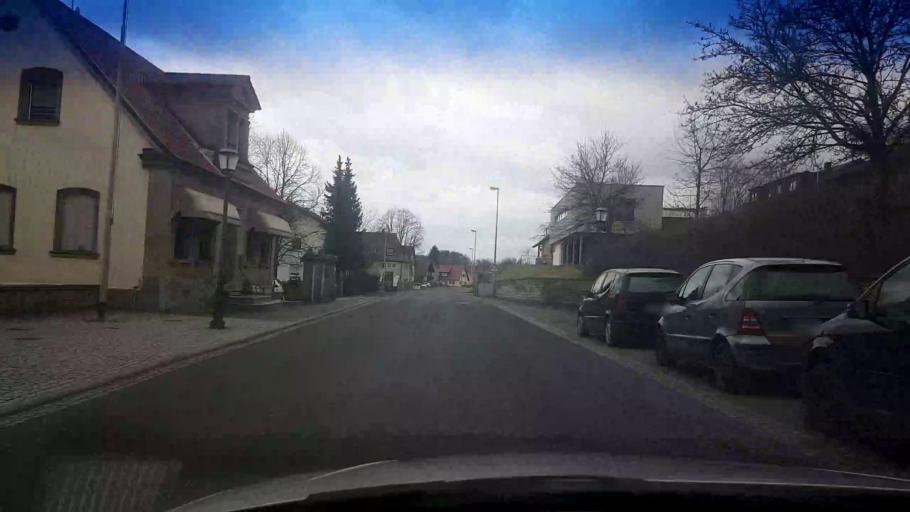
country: DE
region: Bavaria
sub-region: Regierungsbezirk Unterfranken
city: Eltmann
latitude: 49.9290
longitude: 10.6538
